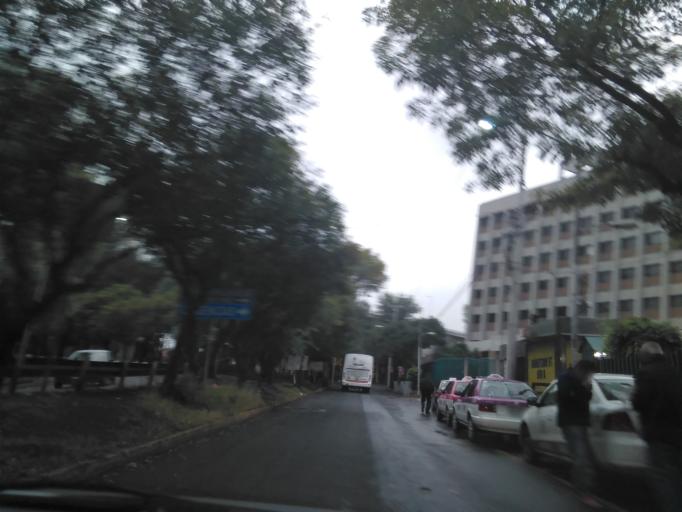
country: MX
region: Mexico City
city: Tlalpan
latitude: 19.2904
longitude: -99.1529
